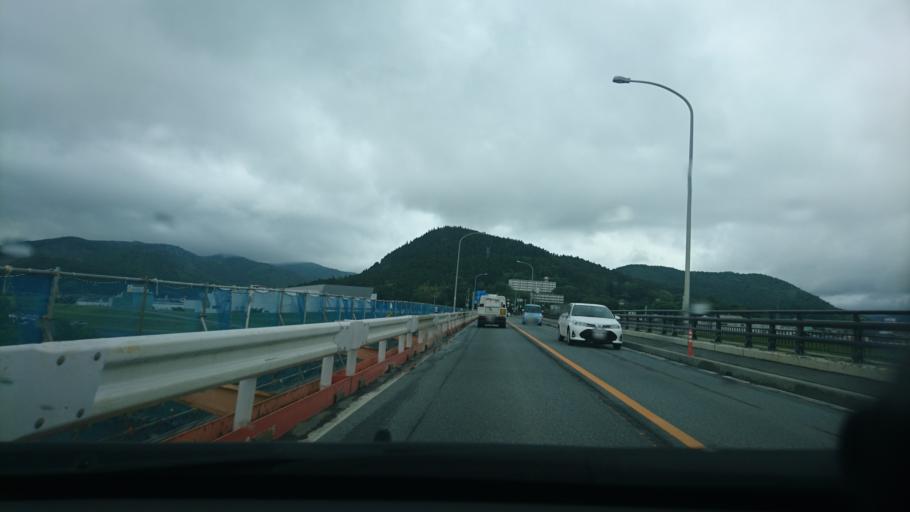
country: JP
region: Miyagi
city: Ishinomaki
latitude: 38.5142
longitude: 141.3081
